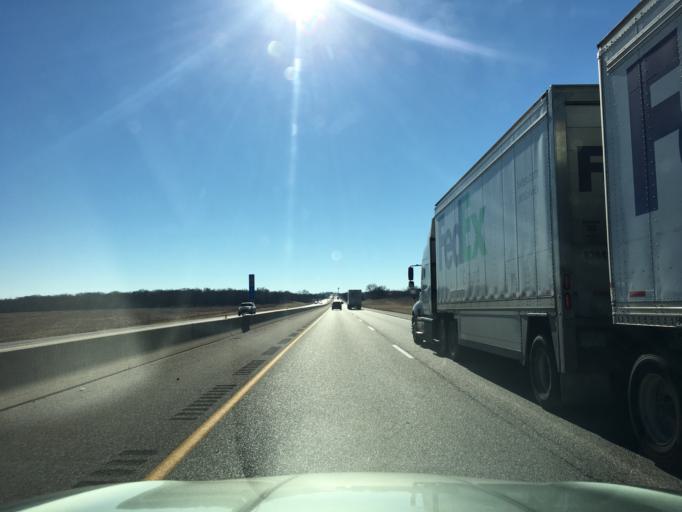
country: US
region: Kansas
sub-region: Sumner County
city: Belle Plaine
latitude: 37.3913
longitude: -97.3255
